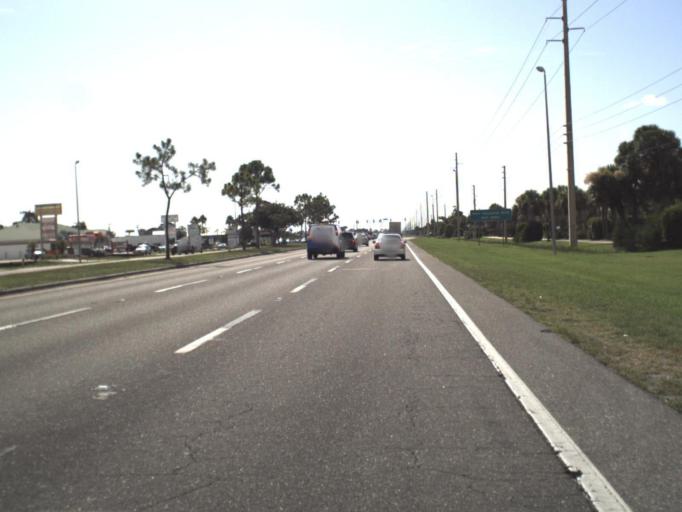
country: US
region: Florida
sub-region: Charlotte County
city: Port Charlotte
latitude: 26.9898
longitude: -82.1098
